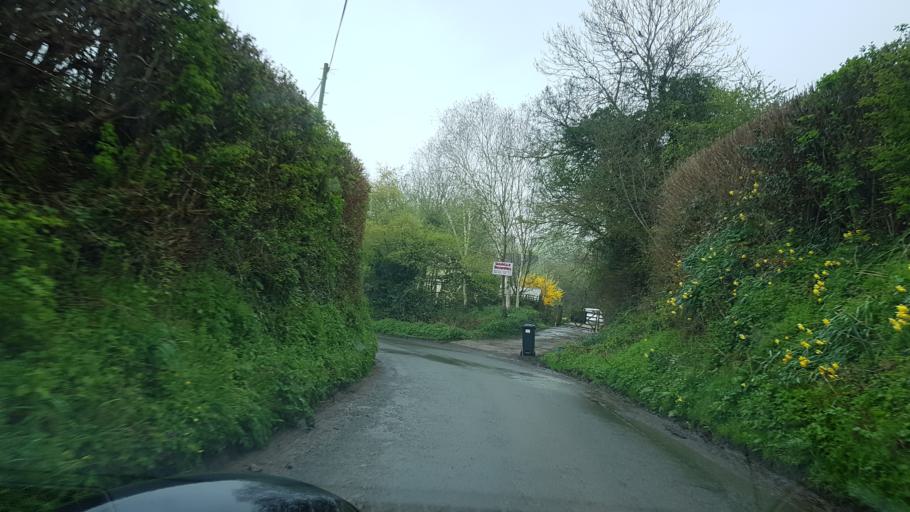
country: GB
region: England
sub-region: Herefordshire
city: Yatton
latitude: 52.0108
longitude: -2.5251
